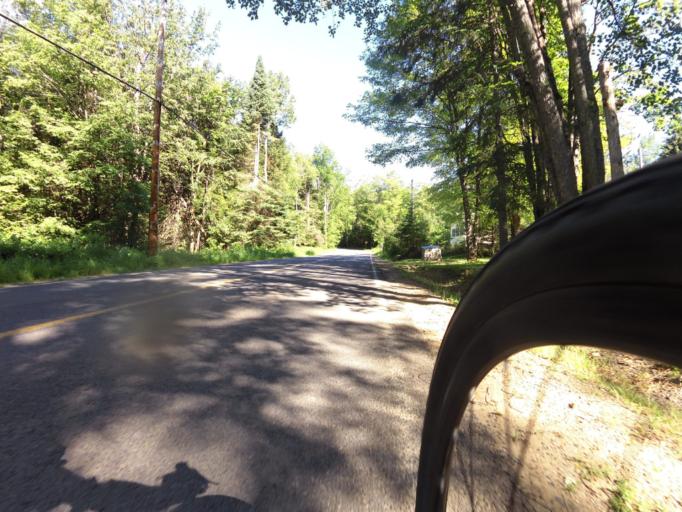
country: CA
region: Quebec
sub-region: Laurentides
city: Brownsburg-Chatham
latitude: 45.8851
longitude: -74.5767
